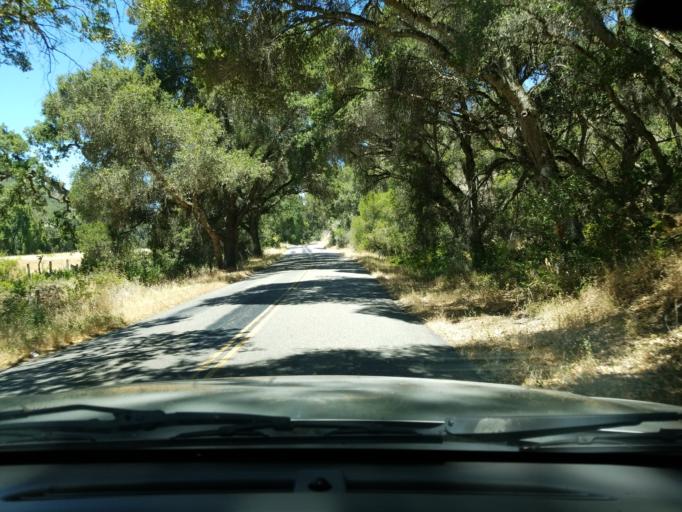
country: US
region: California
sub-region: Monterey County
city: Chualar
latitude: 36.4192
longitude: -121.6091
